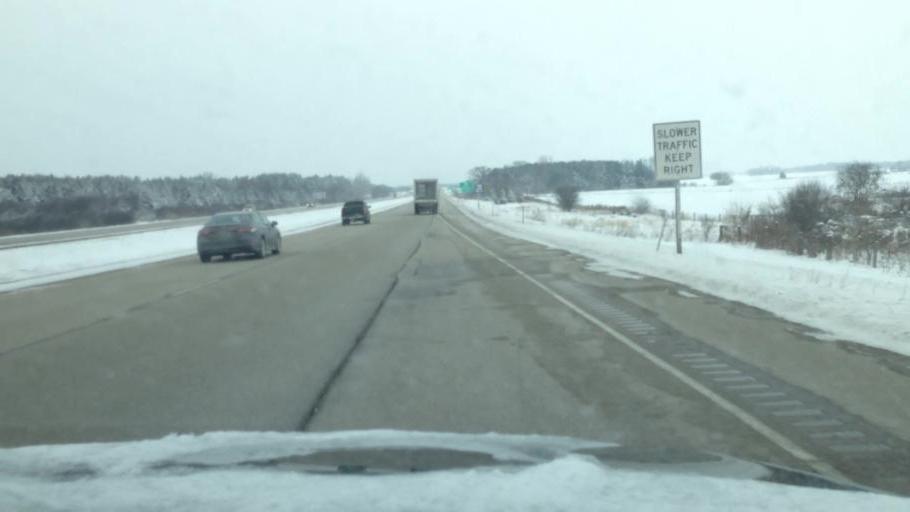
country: US
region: Wisconsin
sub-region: Walworth County
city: Elkhorn
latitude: 42.6780
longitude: -88.5178
